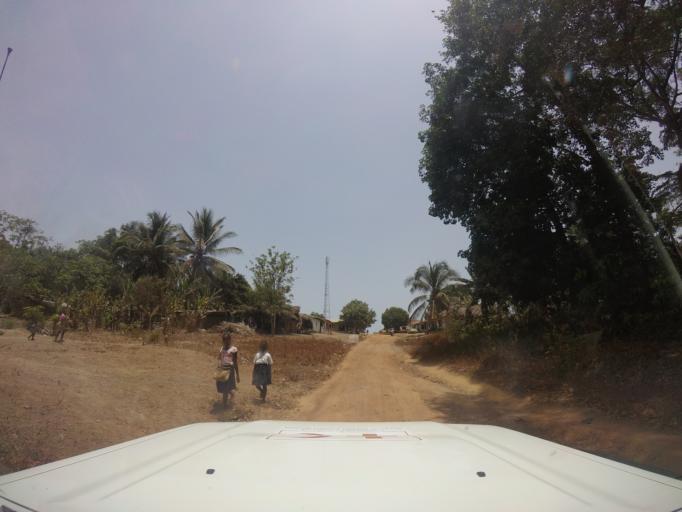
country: LR
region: Grand Cape Mount
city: Robertsport
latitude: 6.9660
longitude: -11.3143
